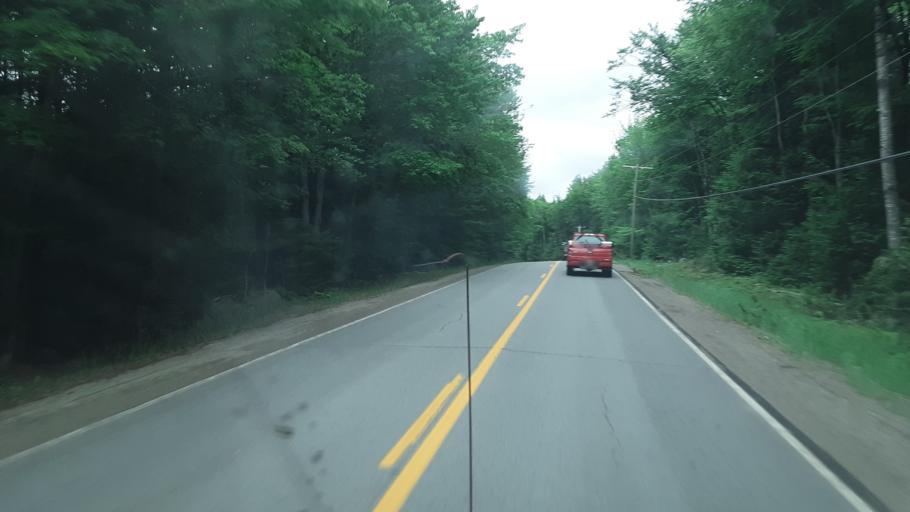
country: US
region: Maine
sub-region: Penobscot County
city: Millinocket
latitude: 45.6787
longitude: -68.7412
